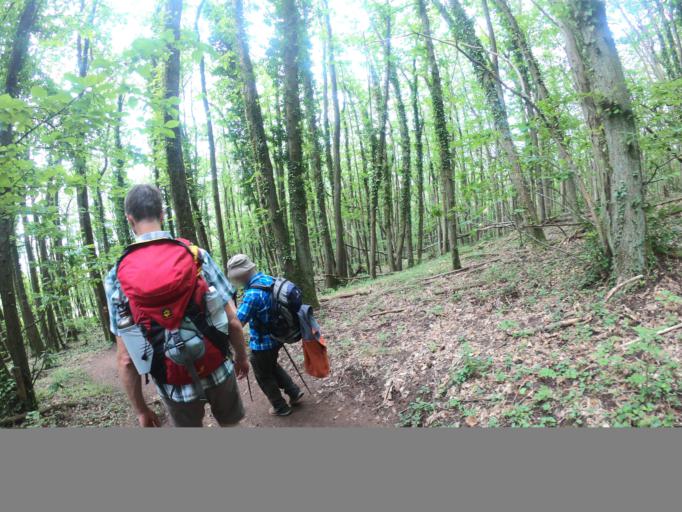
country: DE
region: Rheinland-Pfalz
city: Leinsweiler
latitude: 49.1880
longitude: 8.0160
